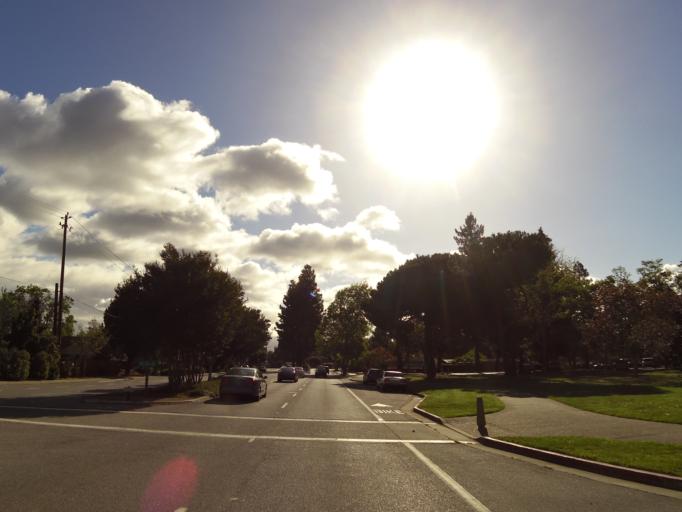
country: US
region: California
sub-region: Santa Clara County
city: Mountain View
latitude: 37.3735
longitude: -122.0804
